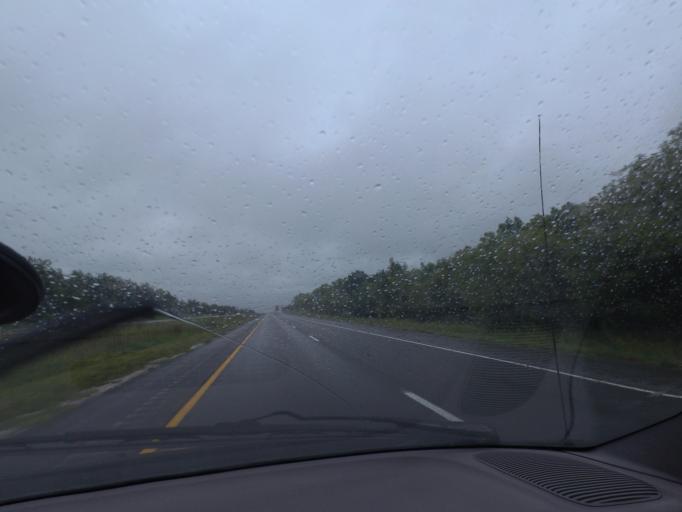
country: US
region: Illinois
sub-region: Scott County
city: Winchester
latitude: 39.6810
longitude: -90.4949
